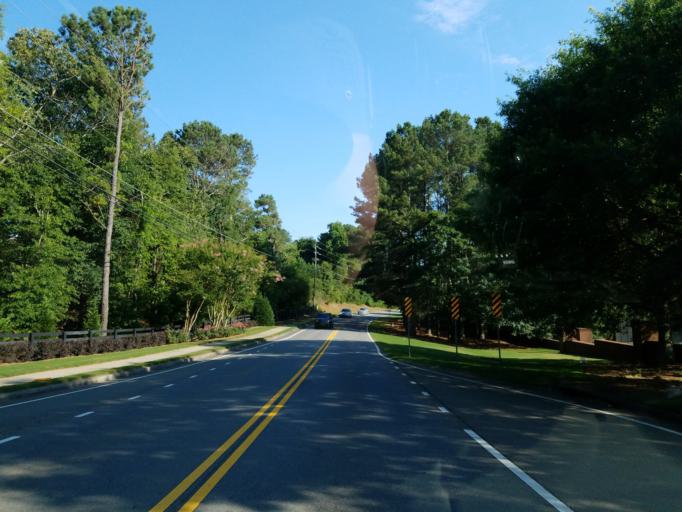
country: US
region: Georgia
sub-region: Fulton County
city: Milton
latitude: 34.1343
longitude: -84.3434
